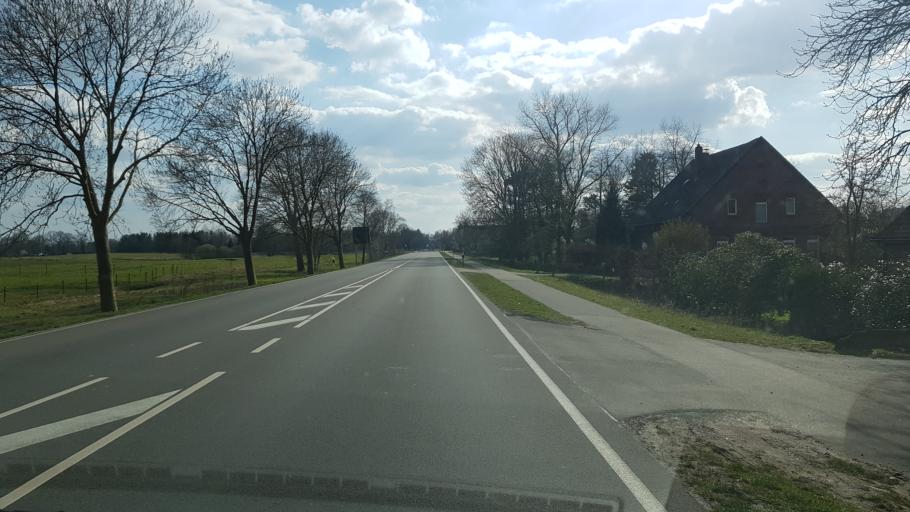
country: DE
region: Lower Saxony
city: Rastede
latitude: 53.2527
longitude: 8.3009
